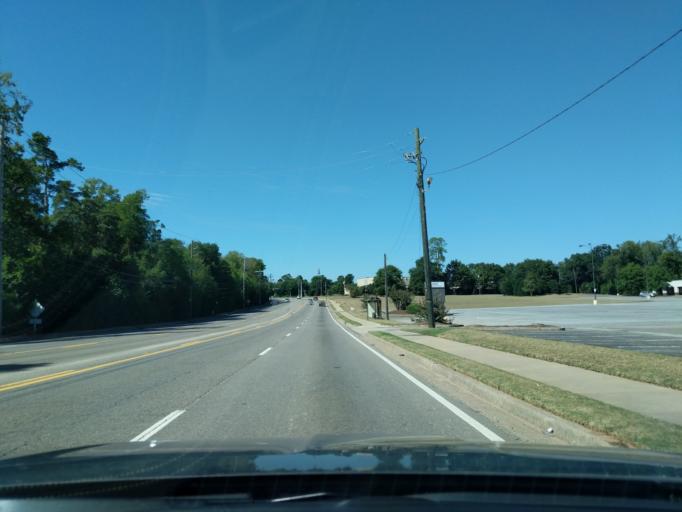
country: US
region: South Carolina
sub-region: Aiken County
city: North Augusta
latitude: 33.5027
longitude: -82.0146
